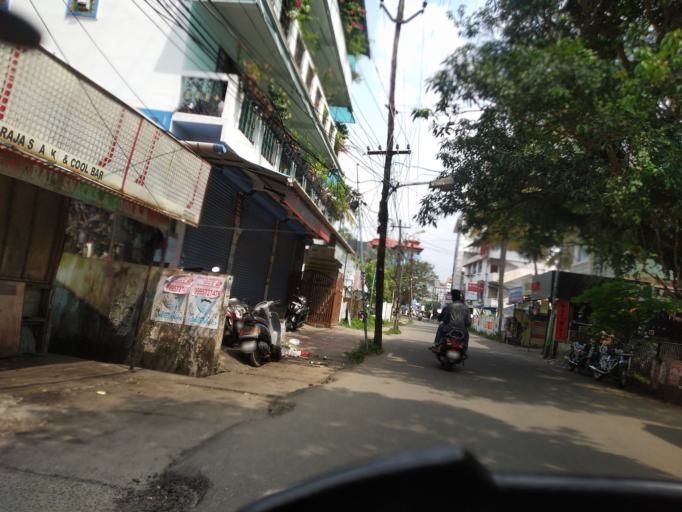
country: IN
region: Kerala
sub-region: Ernakulam
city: Cochin
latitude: 9.9558
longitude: 76.2950
